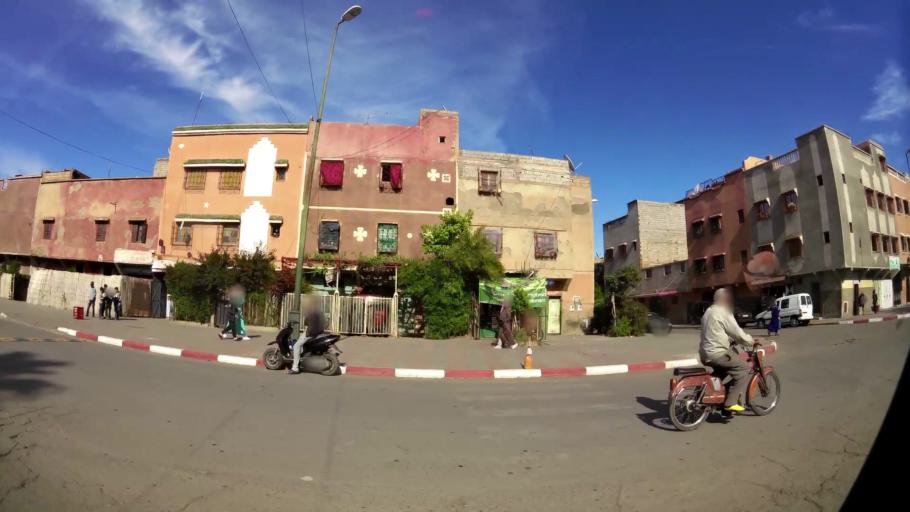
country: MA
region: Marrakech-Tensift-Al Haouz
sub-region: Marrakech
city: Marrakesh
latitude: 31.6079
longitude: -7.9609
